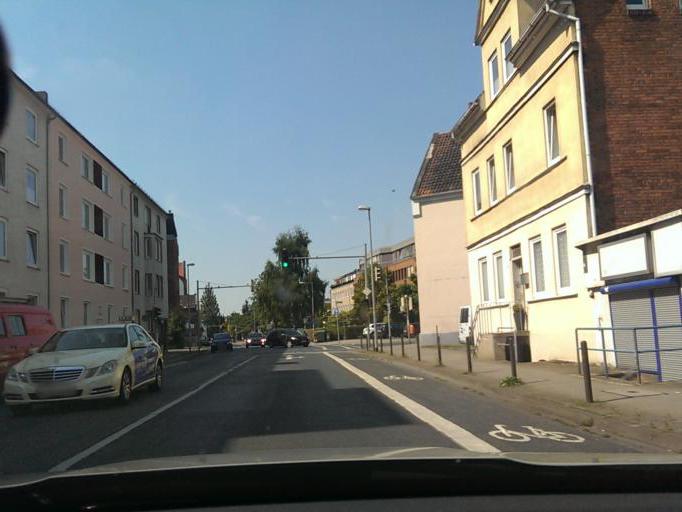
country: DE
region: Lower Saxony
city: Hannover
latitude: 52.3957
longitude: 9.7615
